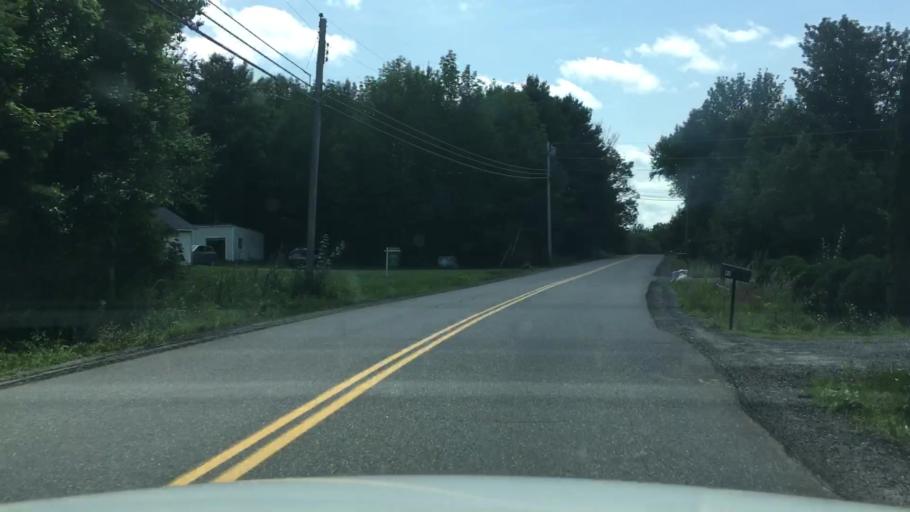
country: US
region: Maine
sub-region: Kennebec County
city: Augusta
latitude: 44.3454
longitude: -69.8090
